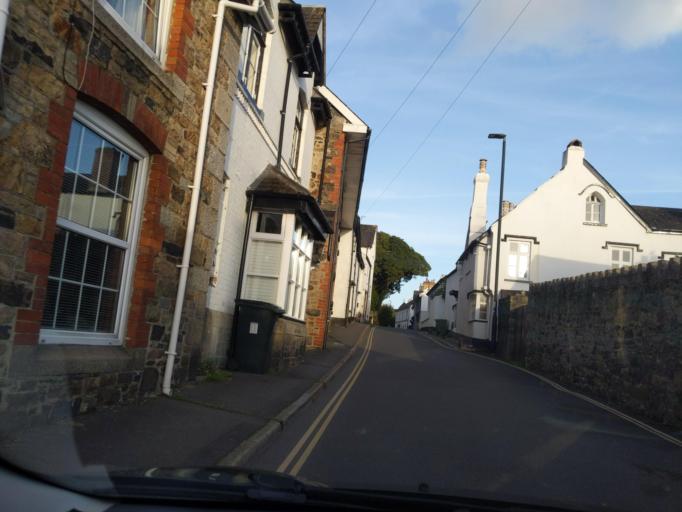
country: GB
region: England
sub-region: Devon
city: Bovey Tracey
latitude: 50.5949
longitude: -3.6711
